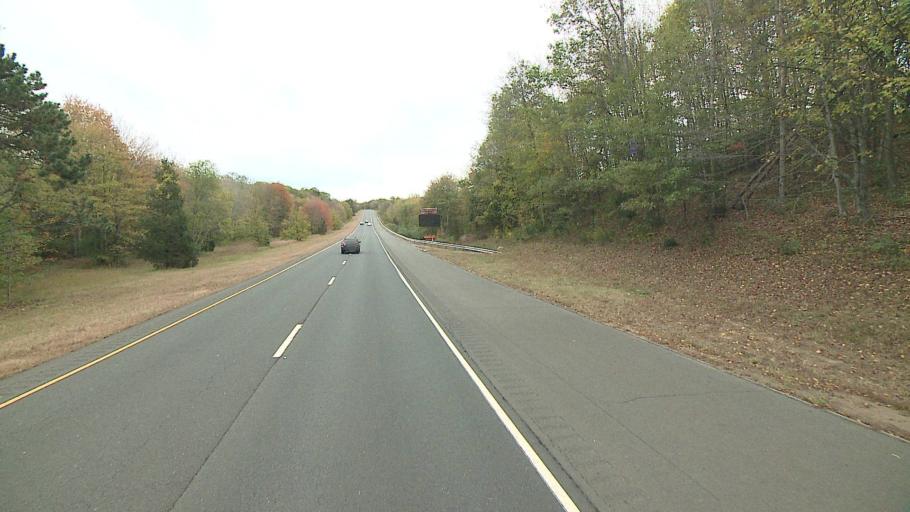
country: US
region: Connecticut
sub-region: Middlesex County
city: East Haddam
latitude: 41.4412
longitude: -72.5183
